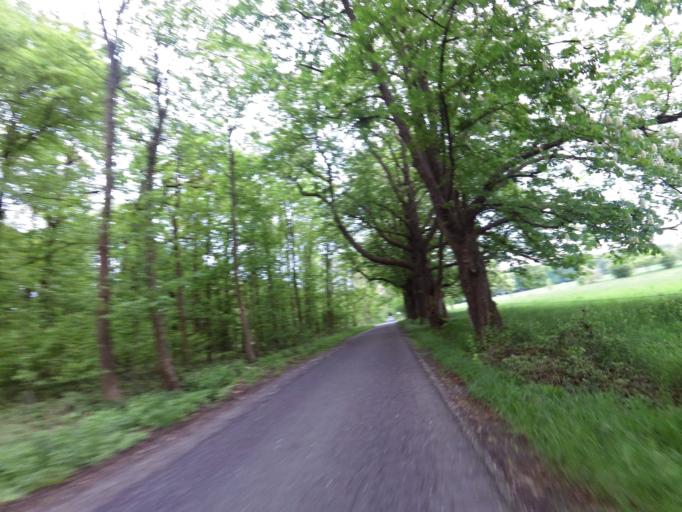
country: DE
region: North Rhine-Westphalia
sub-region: Regierungsbezirk Koln
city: Bonn
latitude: 50.6866
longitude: 7.1094
